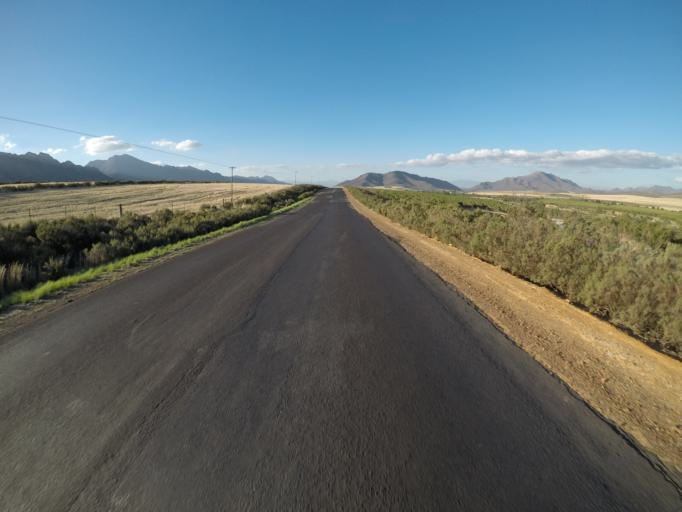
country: ZA
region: Western Cape
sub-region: Cape Winelands District Municipality
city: Worcester
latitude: -33.9102
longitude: 19.3639
